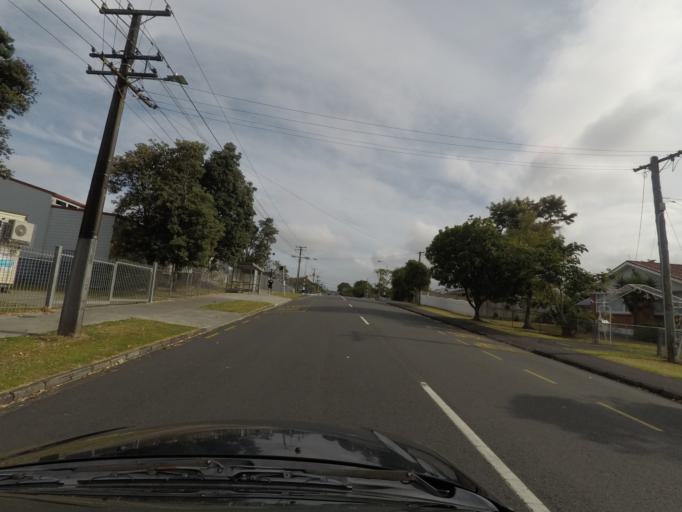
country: NZ
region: Auckland
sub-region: Auckland
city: Waitakere
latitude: -36.9029
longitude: 174.6653
